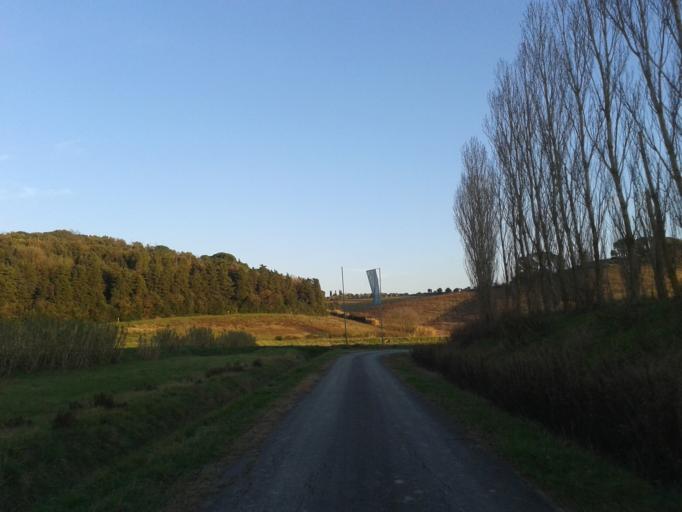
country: IT
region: Tuscany
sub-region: Provincia di Livorno
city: Guasticce
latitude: 43.5918
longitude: 10.4102
